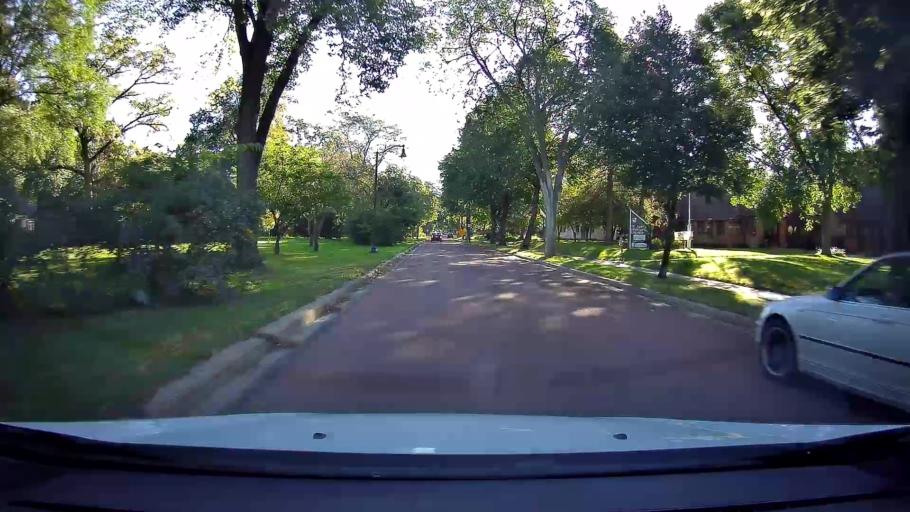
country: US
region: Minnesota
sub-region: Hennepin County
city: Richfield
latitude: 44.9161
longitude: -93.2253
